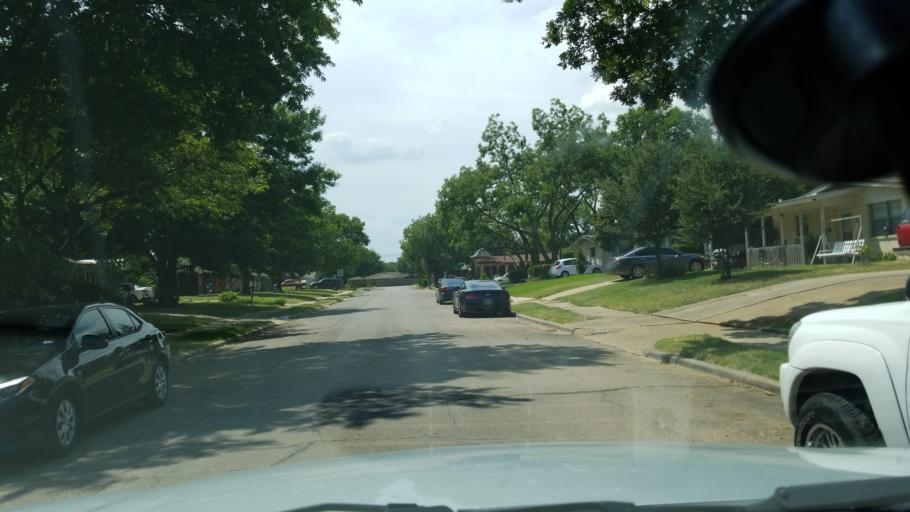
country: US
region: Texas
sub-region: Dallas County
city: Irving
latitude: 32.8241
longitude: -96.9860
